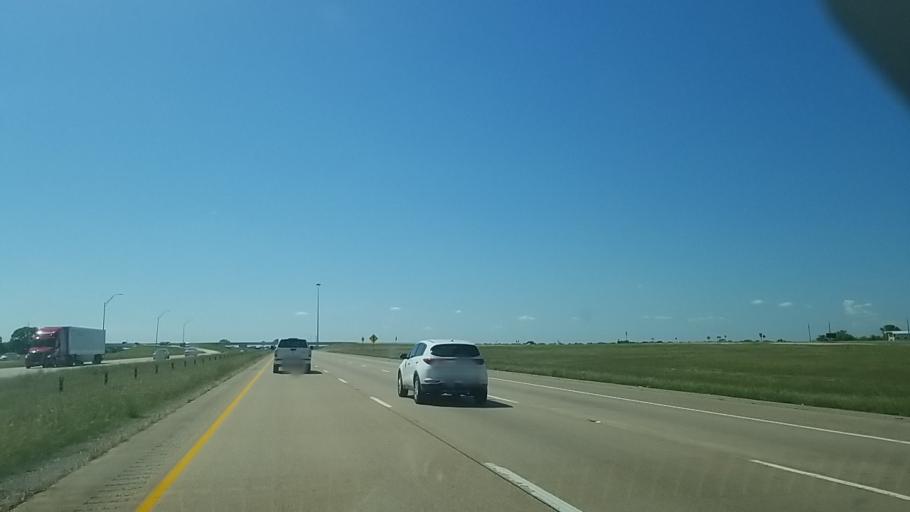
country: US
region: Texas
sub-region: Ellis County
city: Ennis
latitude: 32.2949
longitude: -96.5630
